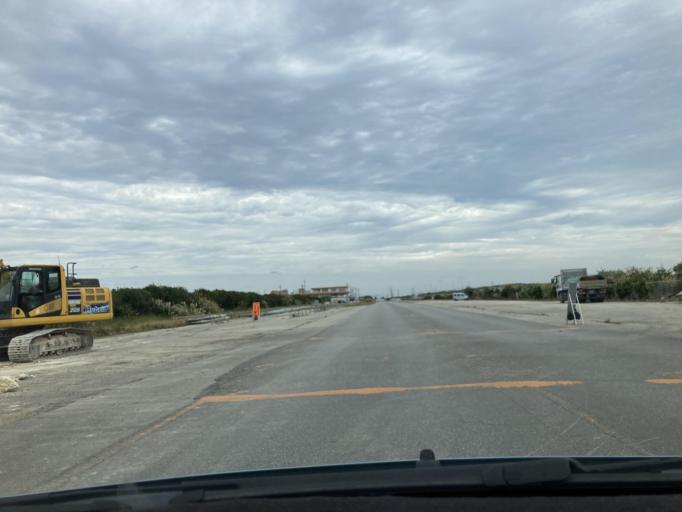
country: JP
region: Okinawa
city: Okinawa
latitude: 26.3894
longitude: 127.7463
